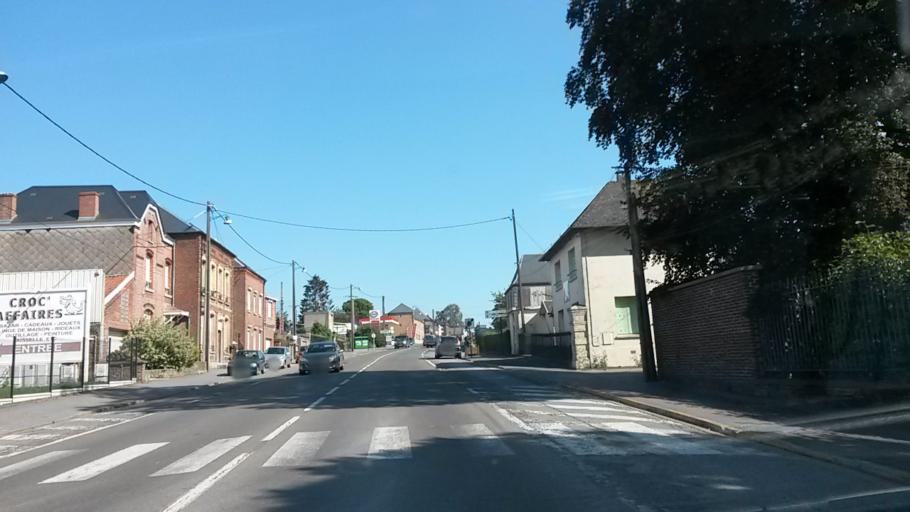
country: FR
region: Nord-Pas-de-Calais
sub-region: Departement du Nord
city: Avesnes-sur-Helpe
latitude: 50.1272
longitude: 3.9361
